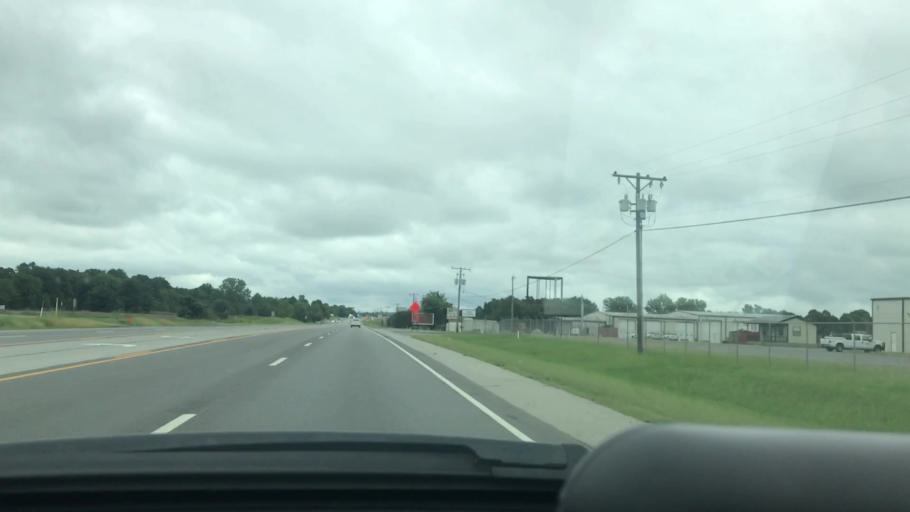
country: US
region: Oklahoma
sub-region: Pittsburg County
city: McAlester
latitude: 34.8783
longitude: -95.7966
